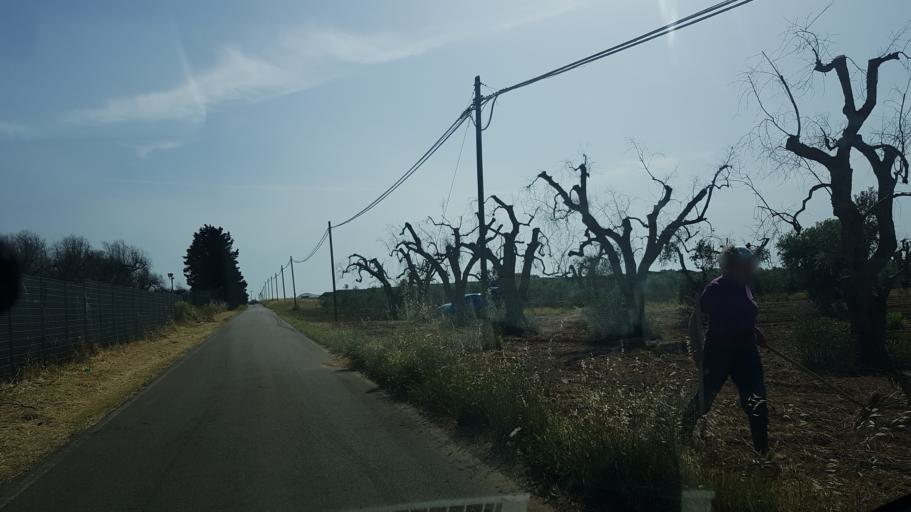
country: IT
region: Apulia
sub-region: Provincia di Brindisi
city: Torchiarolo
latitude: 40.5131
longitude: 18.0783
